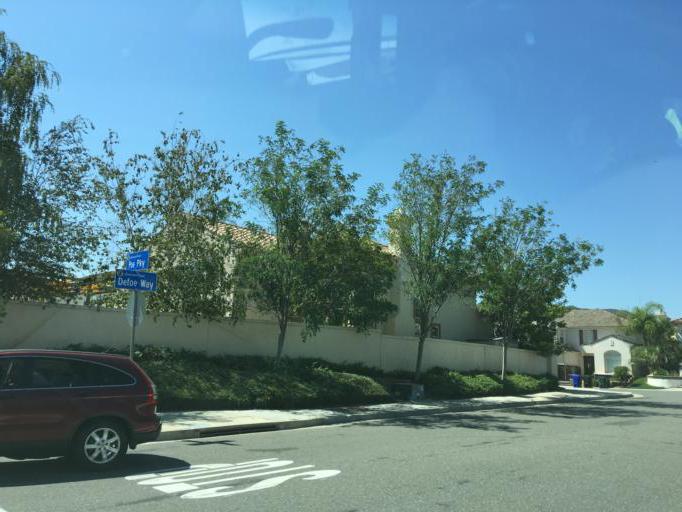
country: US
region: California
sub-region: Los Angeles County
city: Valencia
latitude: 34.3908
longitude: -118.6031
